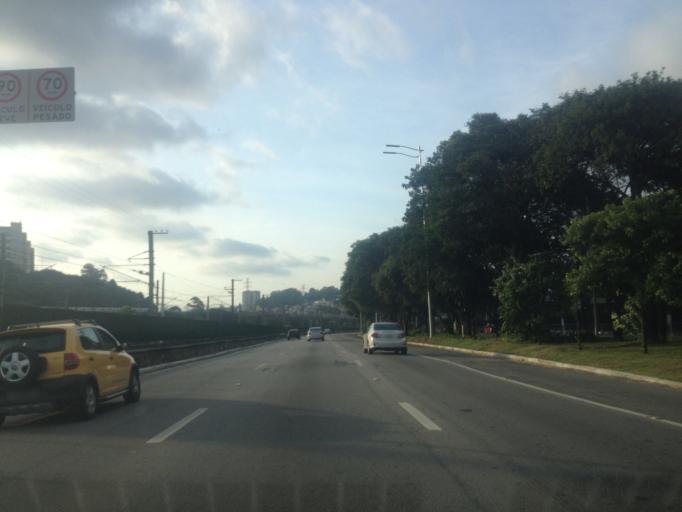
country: BR
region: Sao Paulo
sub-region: Taboao Da Serra
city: Taboao da Serra
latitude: -23.6511
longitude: -46.7234
